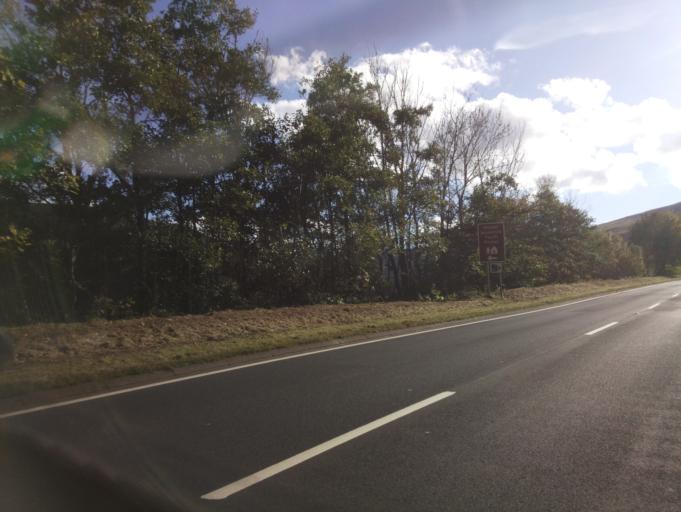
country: GB
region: Wales
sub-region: Sir Powys
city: Brecon
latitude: 51.8950
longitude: -3.4941
